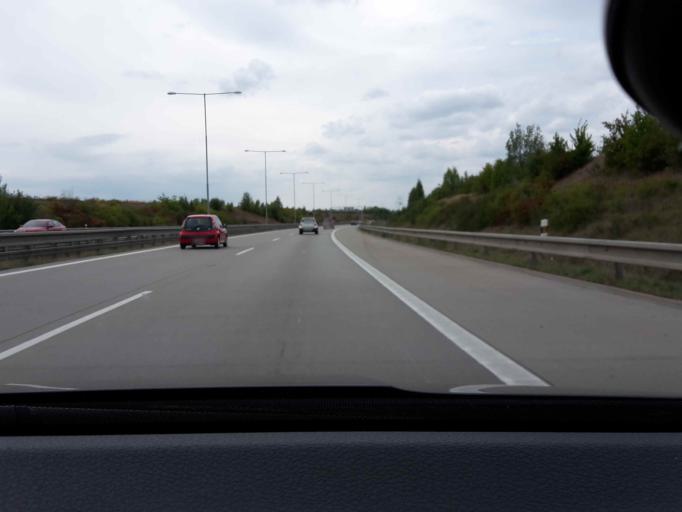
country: CZ
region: Central Bohemia
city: Jesenice
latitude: 49.9640
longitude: 14.4987
